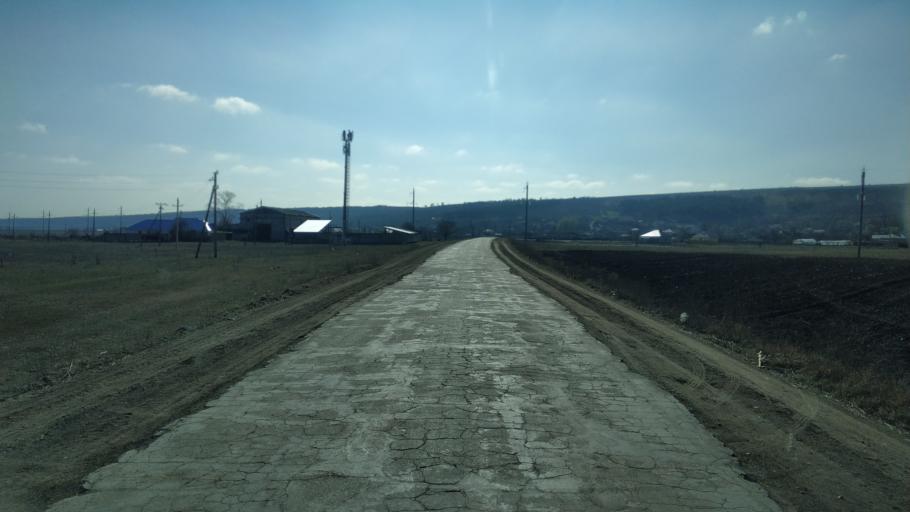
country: MD
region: Hincesti
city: Hincesti
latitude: 46.7537
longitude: 28.6526
